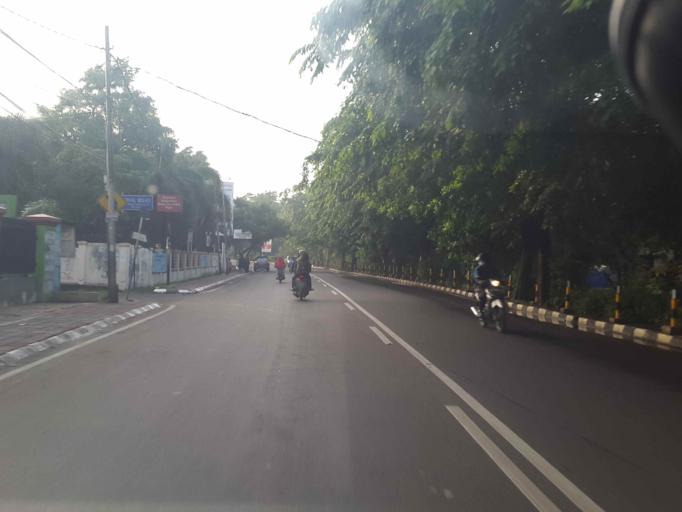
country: ID
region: West Java
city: Bekasi
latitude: -6.2502
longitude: 107.0104
